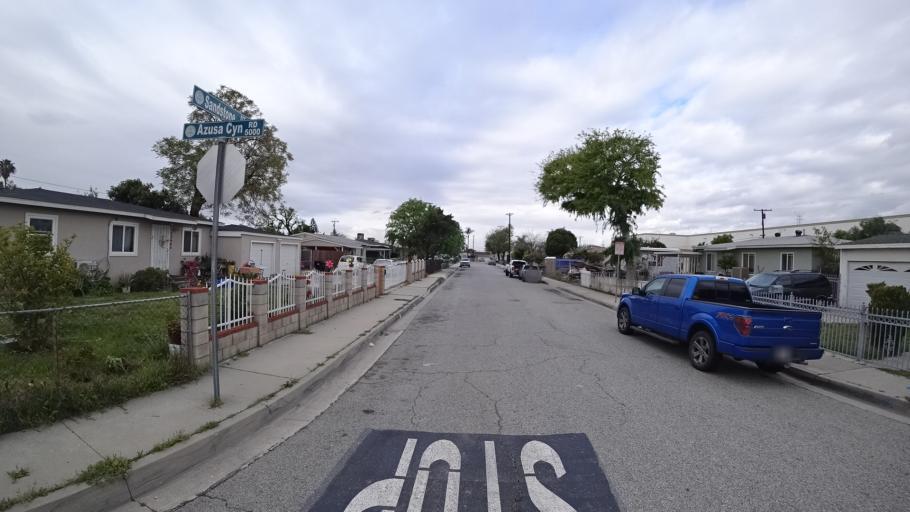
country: US
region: California
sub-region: Los Angeles County
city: Irwindale
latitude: 34.1048
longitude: -117.9432
